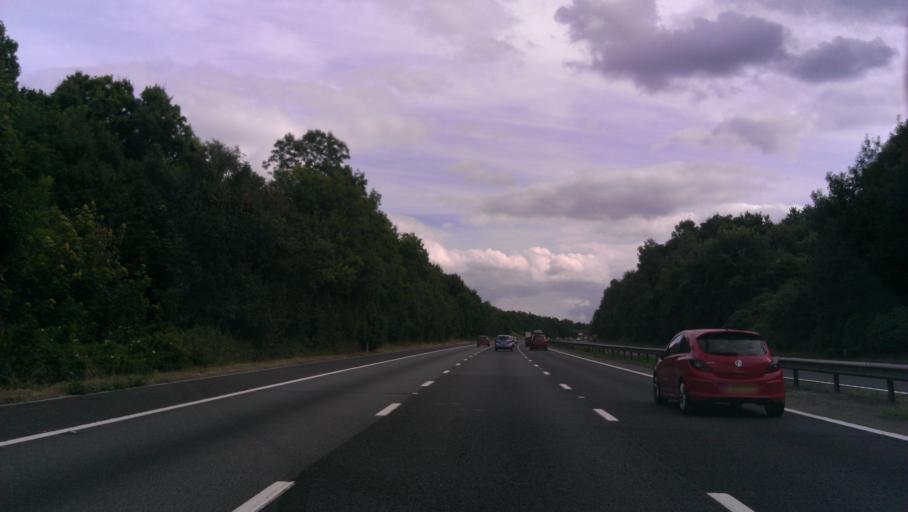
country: GB
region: England
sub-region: Kent
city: Longfield
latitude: 51.3583
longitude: 0.2704
